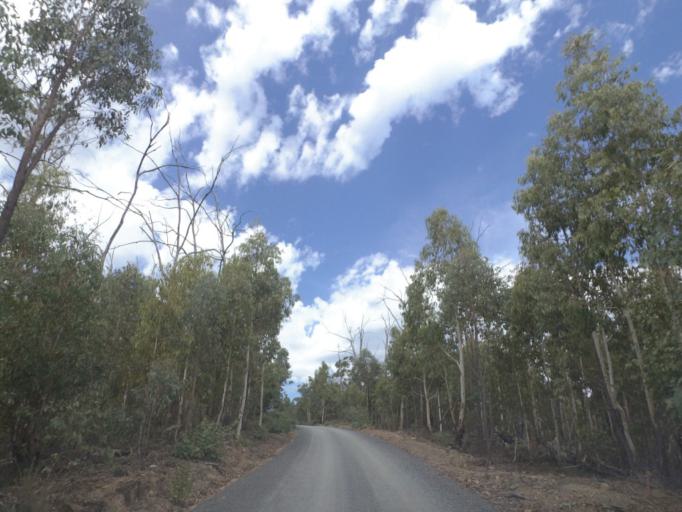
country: AU
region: Victoria
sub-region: Murrindindi
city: Alexandra
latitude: -37.3957
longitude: 145.7564
